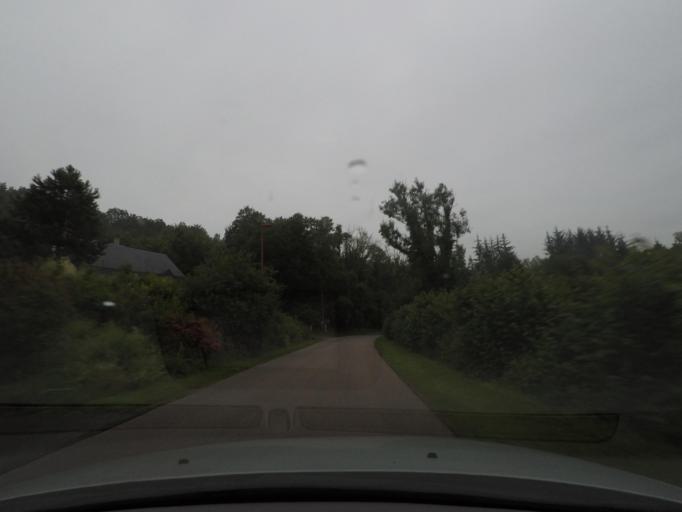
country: FR
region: Haute-Normandie
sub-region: Departement de la Seine-Maritime
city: Fontaine-le-Bourg
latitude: 49.5788
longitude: 1.2108
